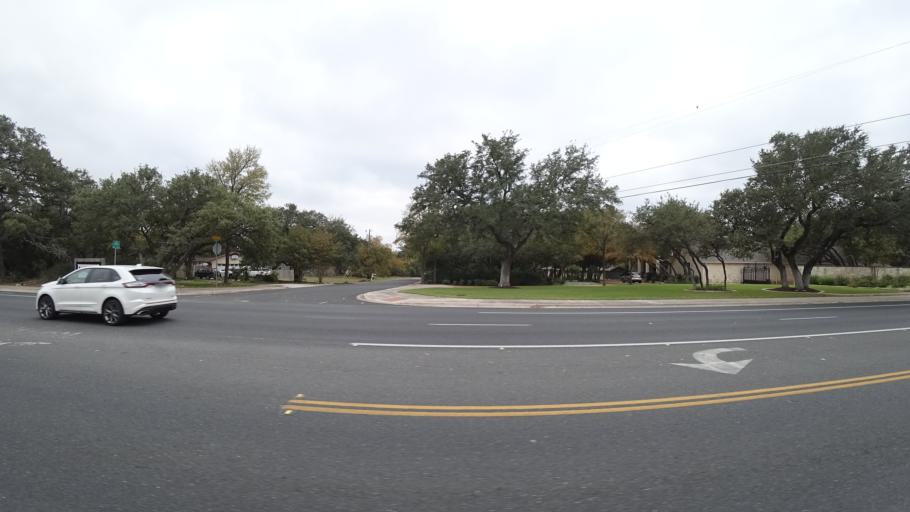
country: US
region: Texas
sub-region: Williamson County
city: Anderson Mill
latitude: 30.4497
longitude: -97.8164
